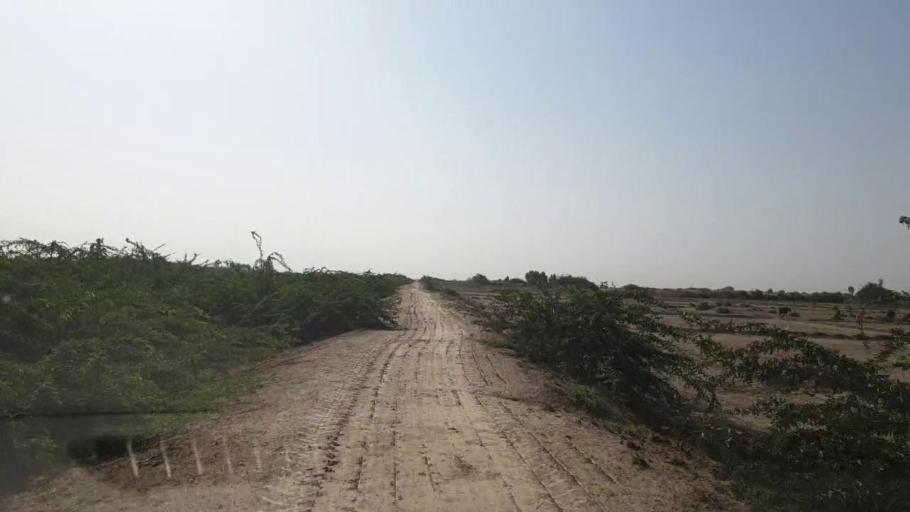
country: PK
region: Sindh
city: Kadhan
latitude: 24.5787
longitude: 69.0803
